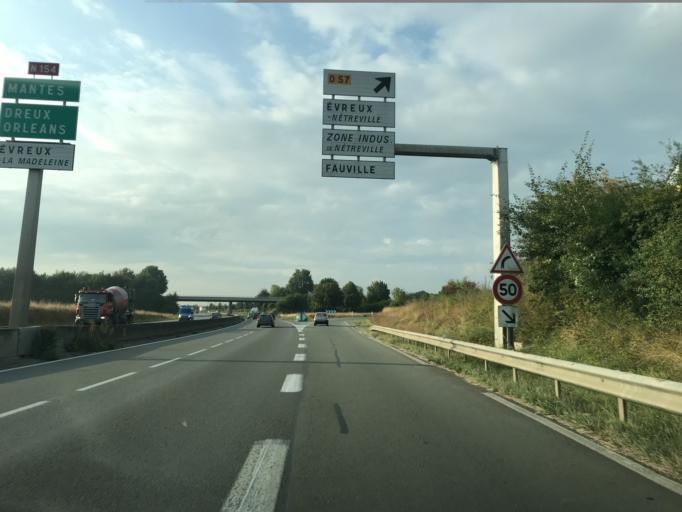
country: FR
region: Haute-Normandie
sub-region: Departement de l'Eure
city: Gravigny
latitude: 49.0310
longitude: 1.1867
